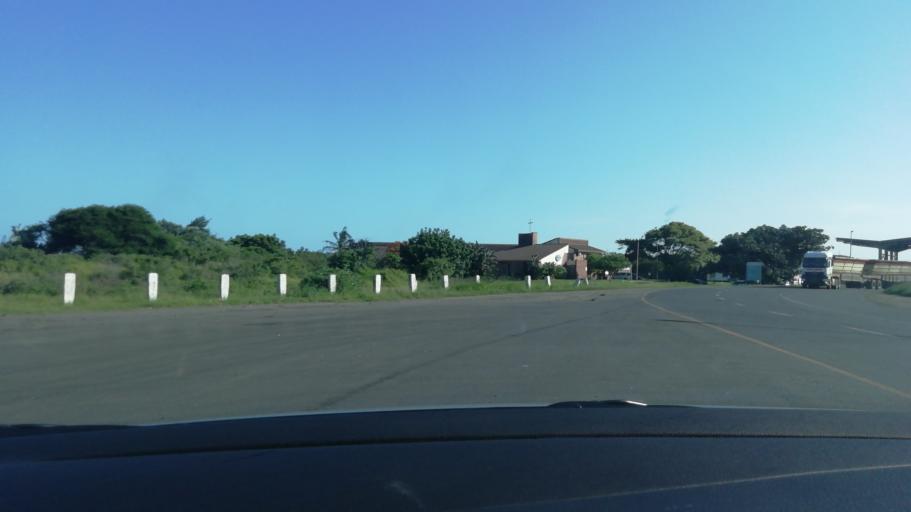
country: ZA
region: KwaZulu-Natal
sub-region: uThungulu District Municipality
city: Richards Bay
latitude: -28.7875
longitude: 32.0269
